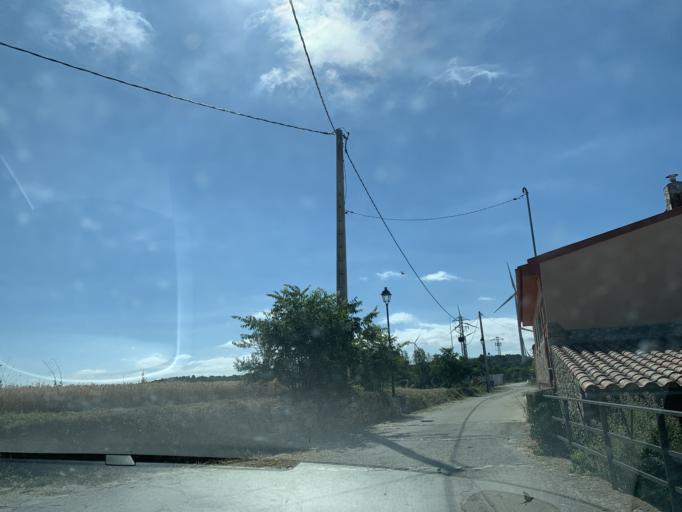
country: ES
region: Catalonia
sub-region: Provincia de Tarragona
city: Vallfogona de Riucorb
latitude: 41.5440
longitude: 1.2674
